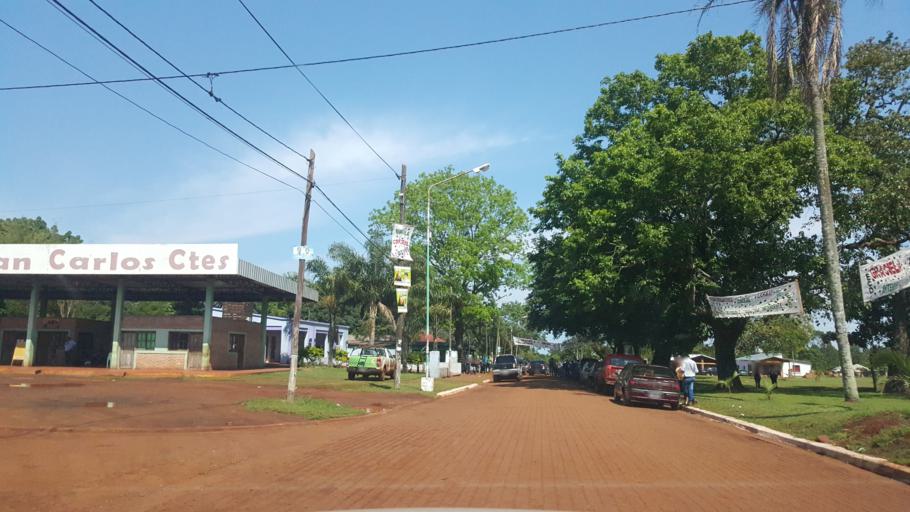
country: AR
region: Corrientes
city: San Carlos
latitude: -27.7443
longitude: -55.9001
